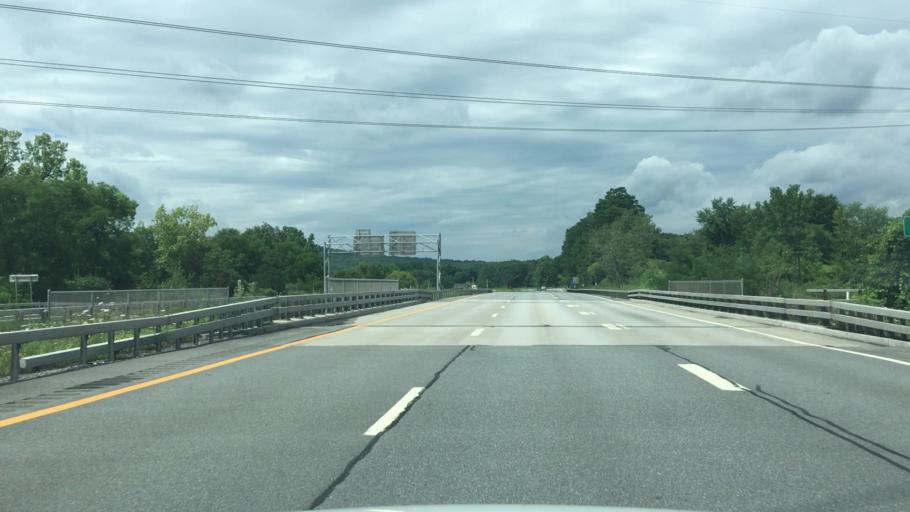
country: US
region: New York
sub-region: Schenectady County
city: Rotterdam
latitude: 42.7806
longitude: -74.0395
